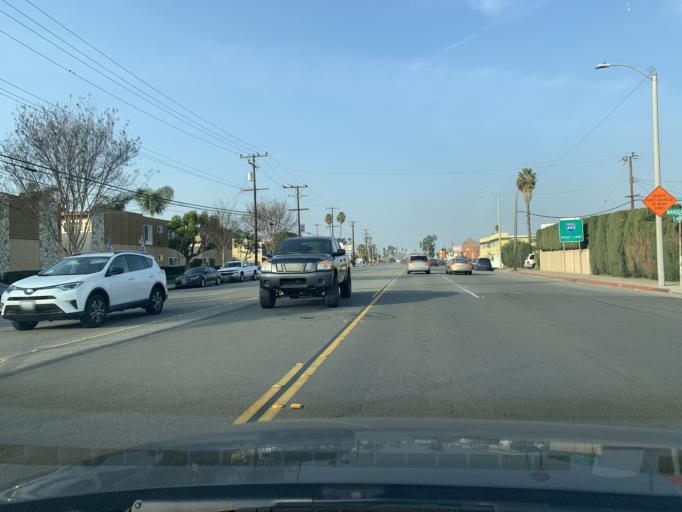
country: US
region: California
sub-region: Orange County
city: Westminster
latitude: 33.7565
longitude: -118.0245
